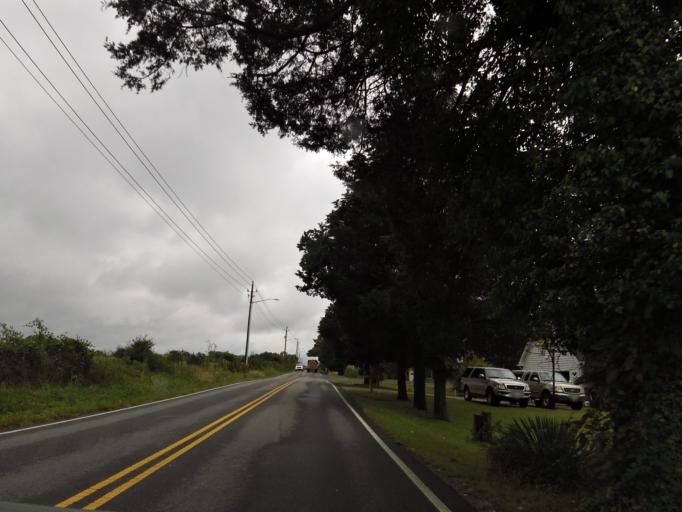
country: US
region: Tennessee
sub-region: Bradley County
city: Hopewell
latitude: 35.2054
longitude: -84.9041
